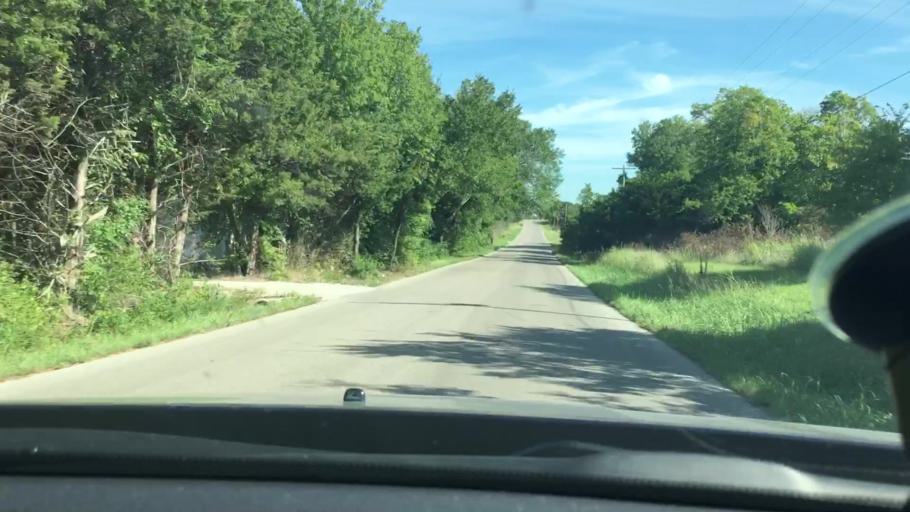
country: US
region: Oklahoma
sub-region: Carter County
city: Lone Grove
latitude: 34.2313
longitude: -97.2475
